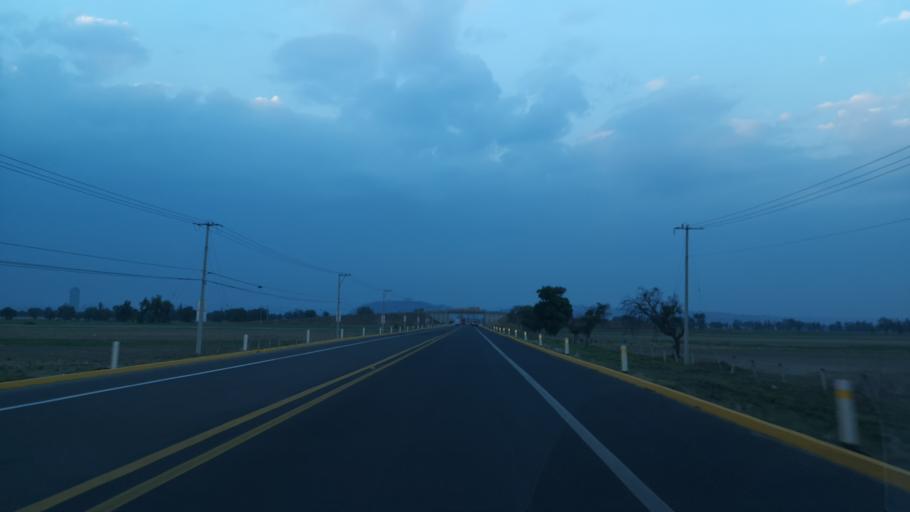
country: MX
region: Puebla
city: Santa Ana Xalmimilulco
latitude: 19.1903
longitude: -98.3679
